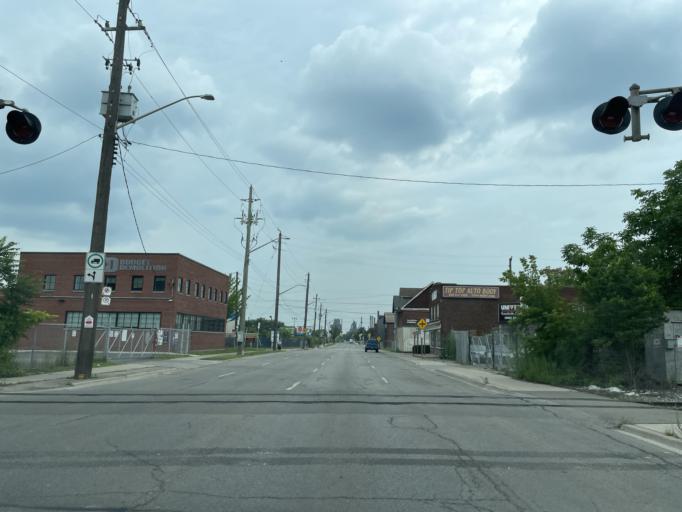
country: CA
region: Ontario
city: Hamilton
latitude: 43.2627
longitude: -79.8335
